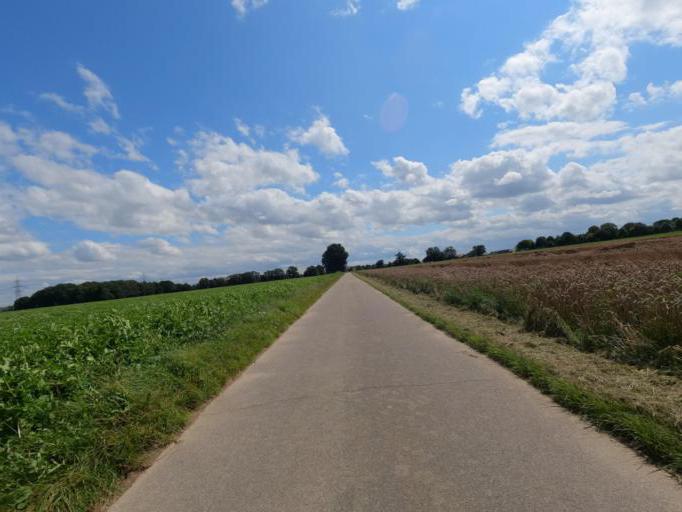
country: DE
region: North Rhine-Westphalia
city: Baesweiler
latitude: 50.9426
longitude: 6.2034
